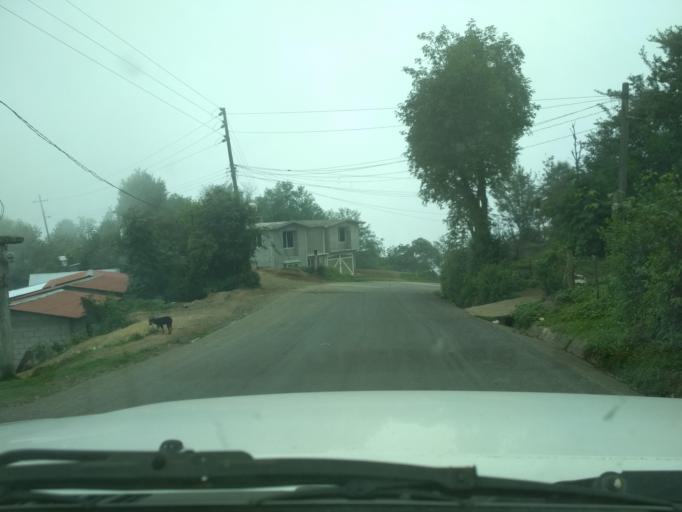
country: MX
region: Veracruz
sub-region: La Perla
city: Chilapa
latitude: 18.9674
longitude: -97.1718
